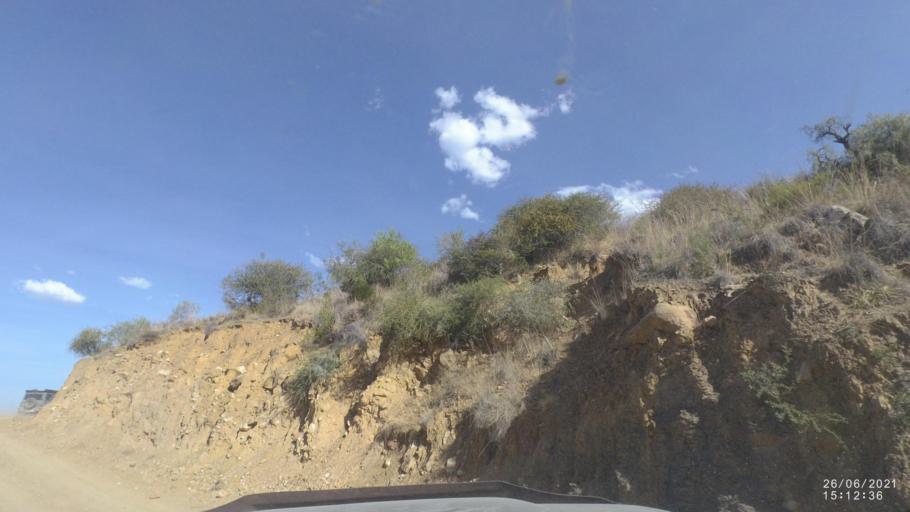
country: BO
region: Cochabamba
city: Mizque
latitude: -17.9585
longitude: -65.6442
